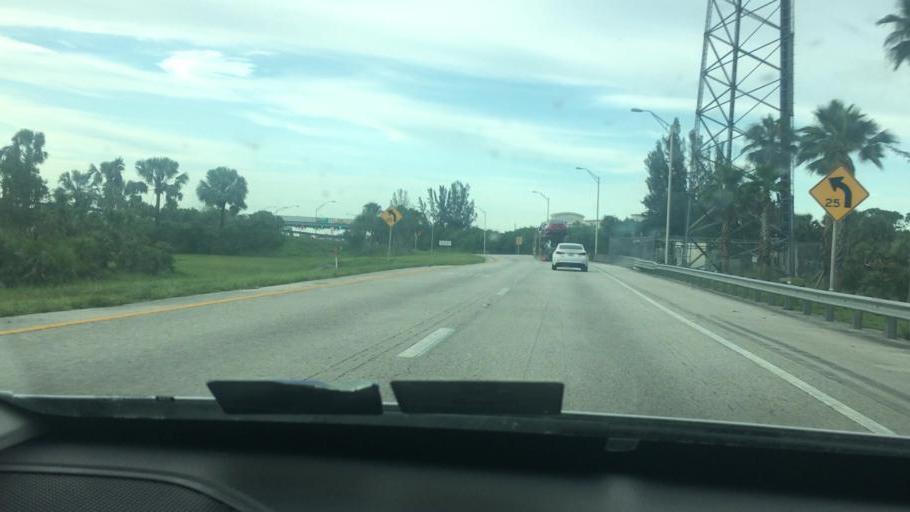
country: US
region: Florida
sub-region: Saint Lucie County
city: Fort Pierce South
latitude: 27.4079
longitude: -80.3986
